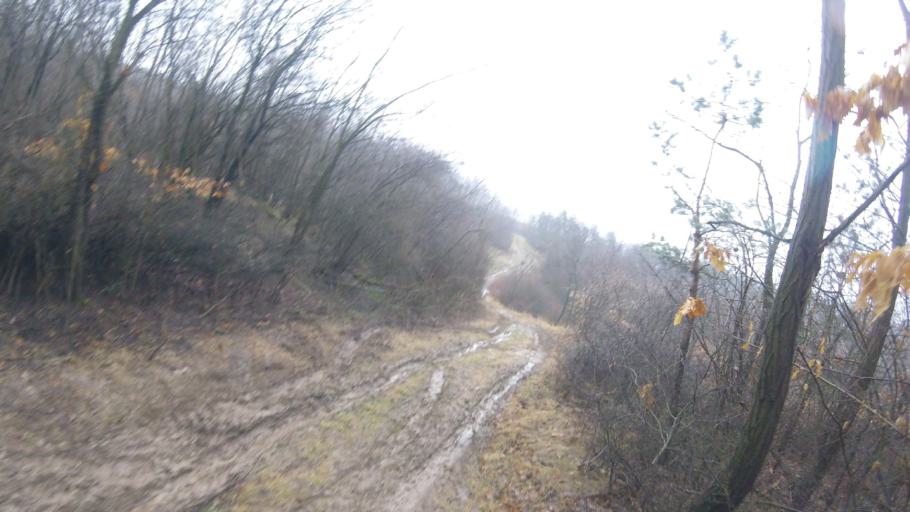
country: HU
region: Borsod-Abauj-Zemplen
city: Saly
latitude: 47.9697
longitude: 20.6252
